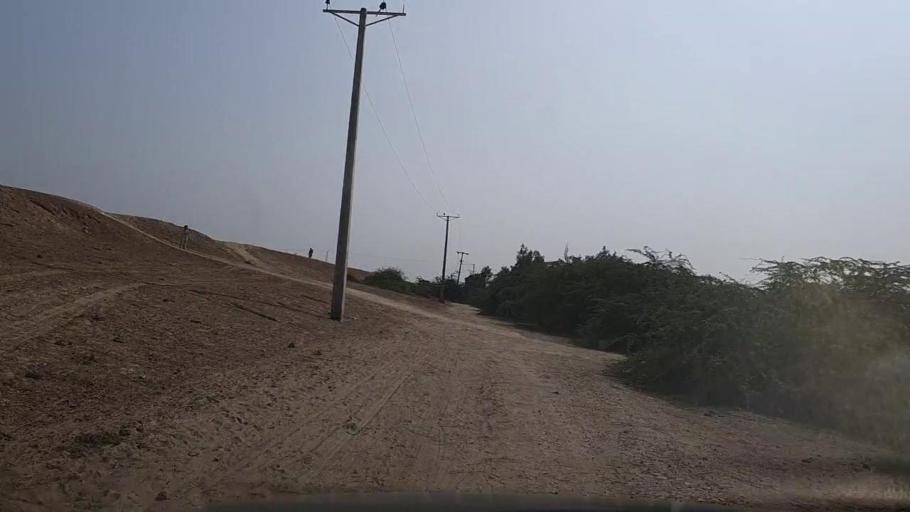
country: PK
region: Sindh
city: Chuhar Jamali
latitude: 24.5532
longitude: 67.9175
